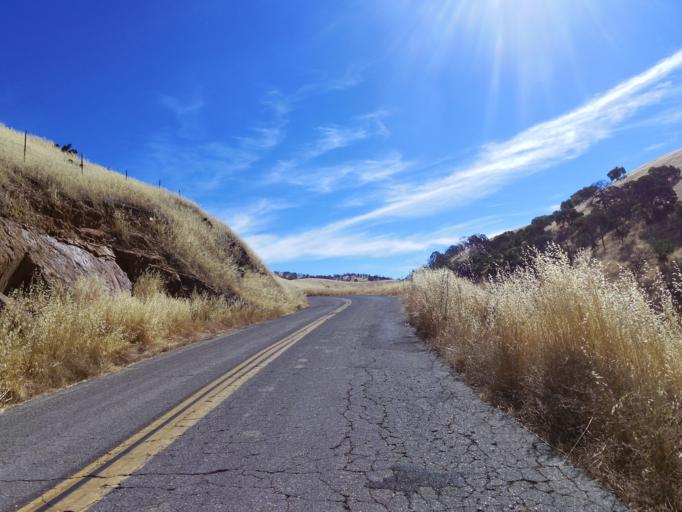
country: US
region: California
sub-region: Mariposa County
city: Mariposa
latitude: 37.3356
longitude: -119.9652
